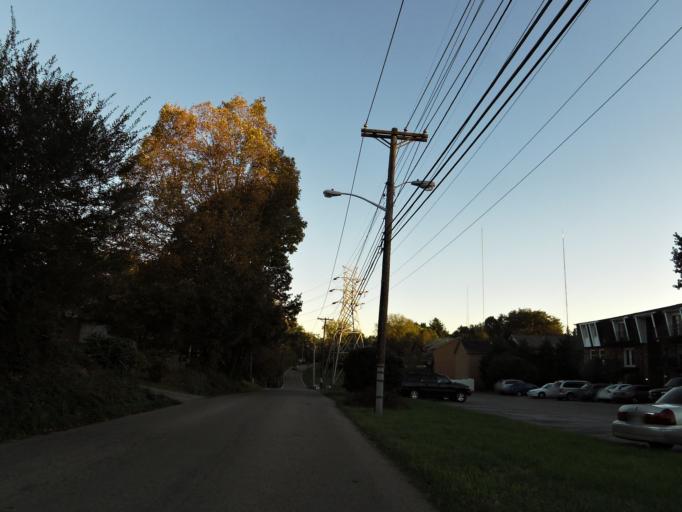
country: US
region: Tennessee
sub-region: Knox County
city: Knoxville
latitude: 36.0221
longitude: -83.9448
